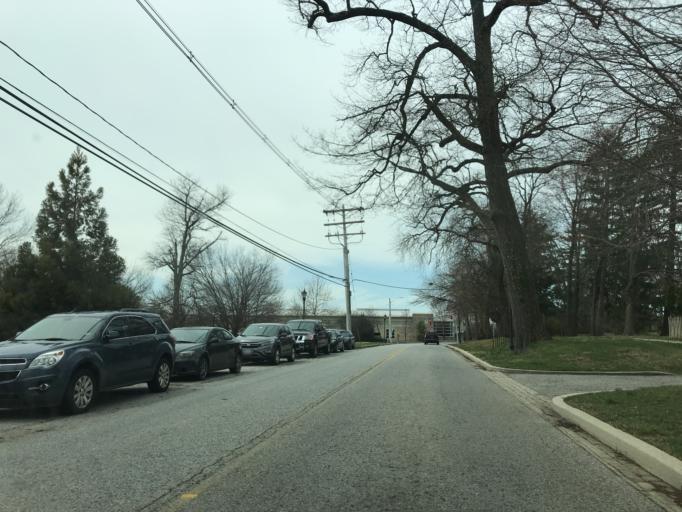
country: US
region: Maryland
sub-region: Baltimore County
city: Towson
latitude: 39.3534
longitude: -76.6219
